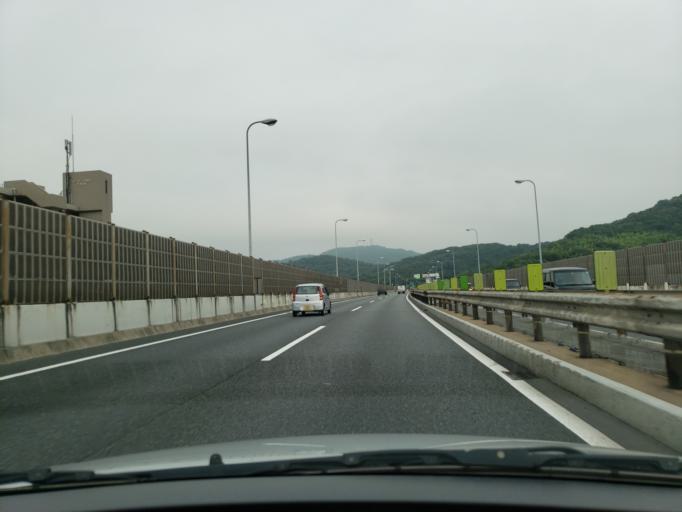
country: JP
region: Hyogo
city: Himeji
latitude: 34.8161
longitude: 134.6529
